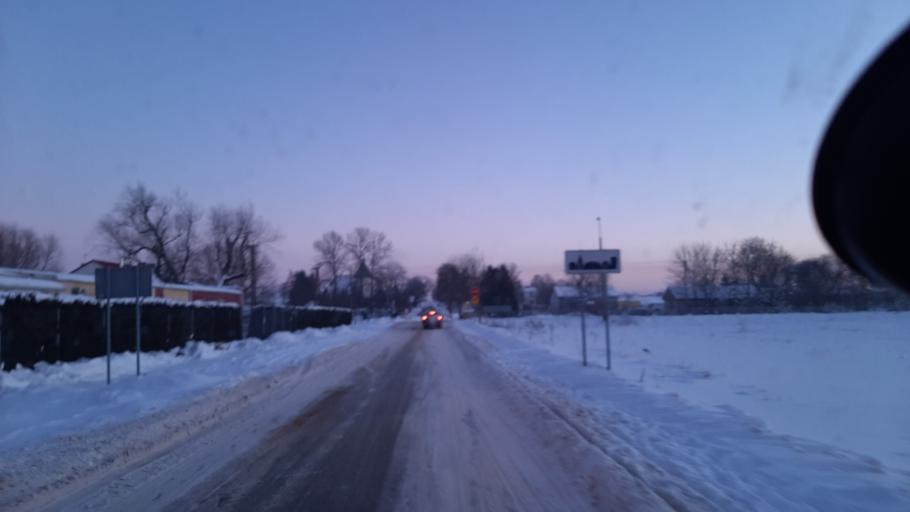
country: PL
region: Lublin Voivodeship
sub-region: Powiat lubelski
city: Niemce
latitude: 51.3633
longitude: 22.5289
